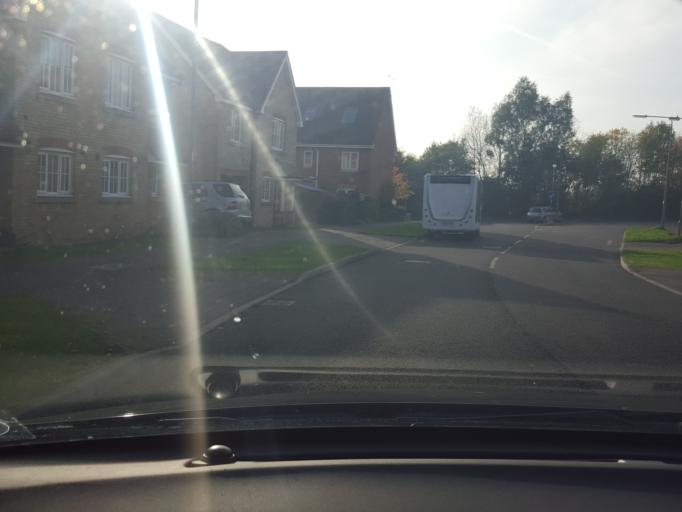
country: GB
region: England
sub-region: Essex
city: Dovercourt
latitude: 51.9260
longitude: 1.2479
